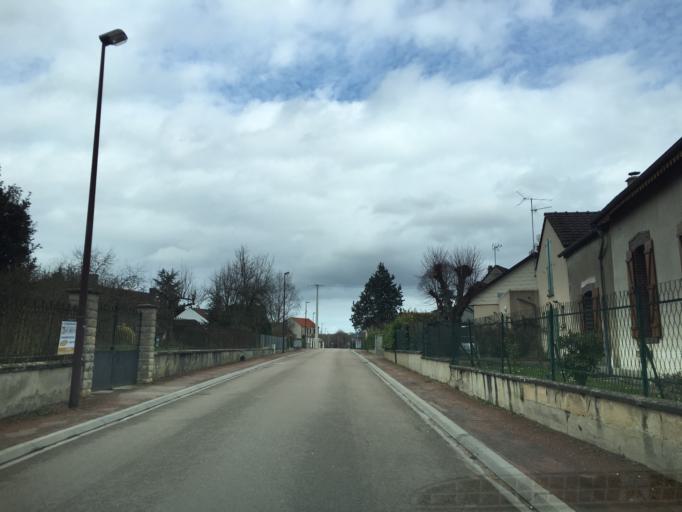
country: FR
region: Bourgogne
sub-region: Departement de l'Yonne
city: Charbuy
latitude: 47.8295
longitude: 3.4590
